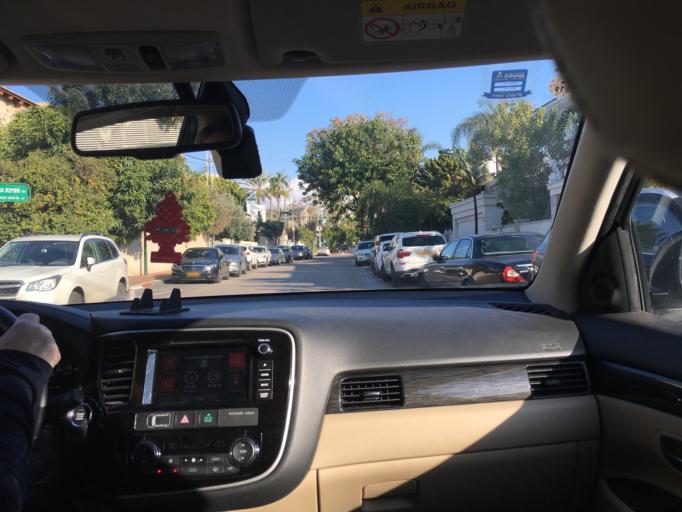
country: IL
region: Tel Aviv
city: Ramat HaSharon
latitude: 32.1509
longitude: 34.8315
